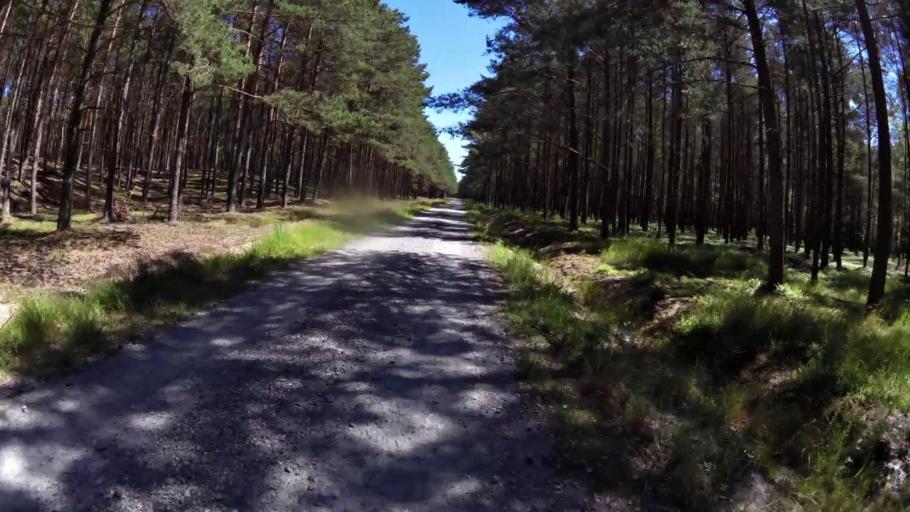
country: PL
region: West Pomeranian Voivodeship
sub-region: Powiat gryficki
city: Trzebiatow
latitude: 54.1041
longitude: 15.1768
